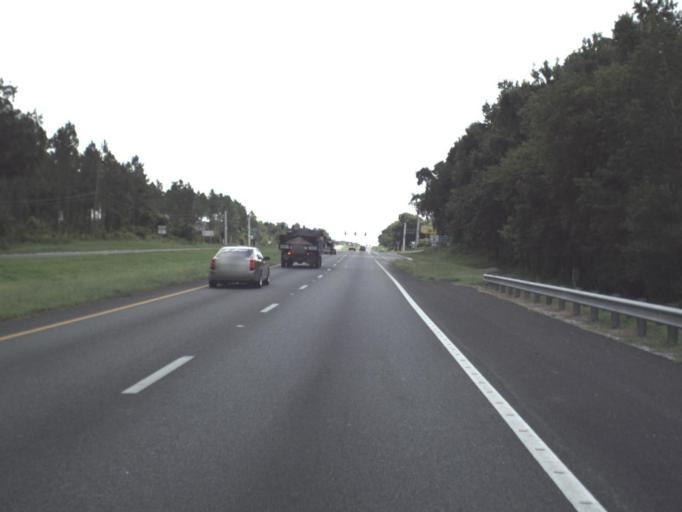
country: US
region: Florida
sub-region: Hernando County
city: Hill 'n Dale
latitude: 28.5231
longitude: -82.3064
